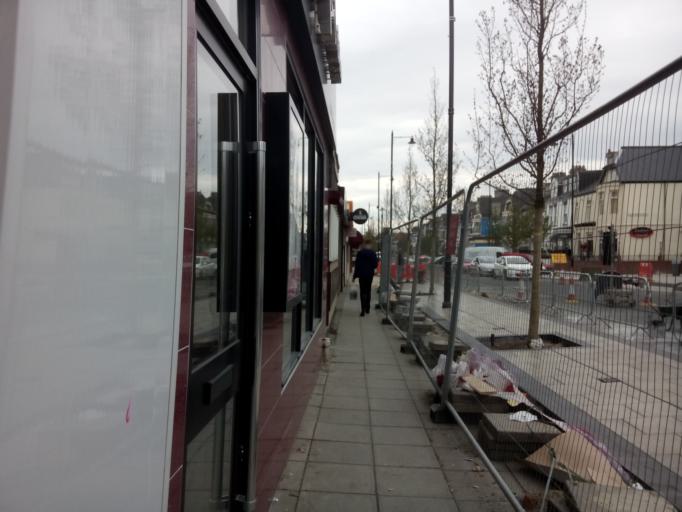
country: GB
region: England
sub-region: South Tyneside
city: South Shields
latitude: 55.0007
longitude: -1.4238
